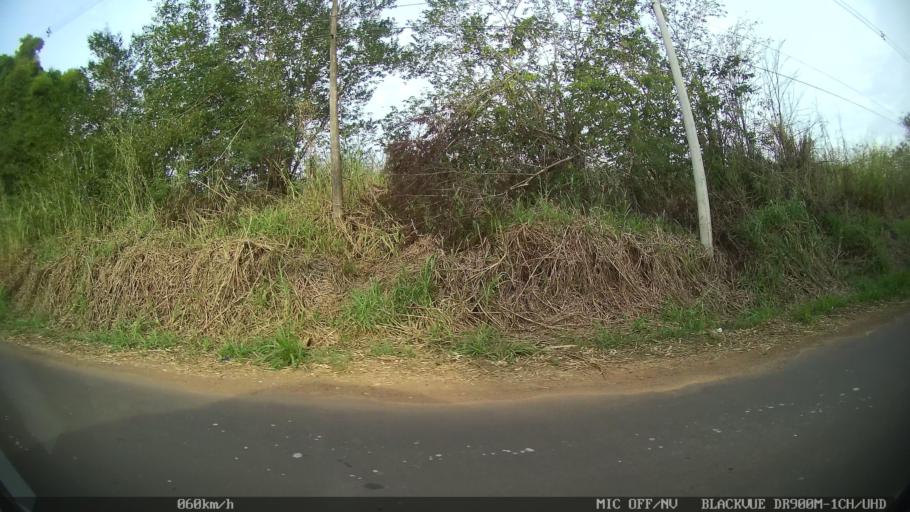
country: BR
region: Sao Paulo
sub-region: Piracicaba
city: Piracicaba
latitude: -22.6966
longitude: -47.5870
